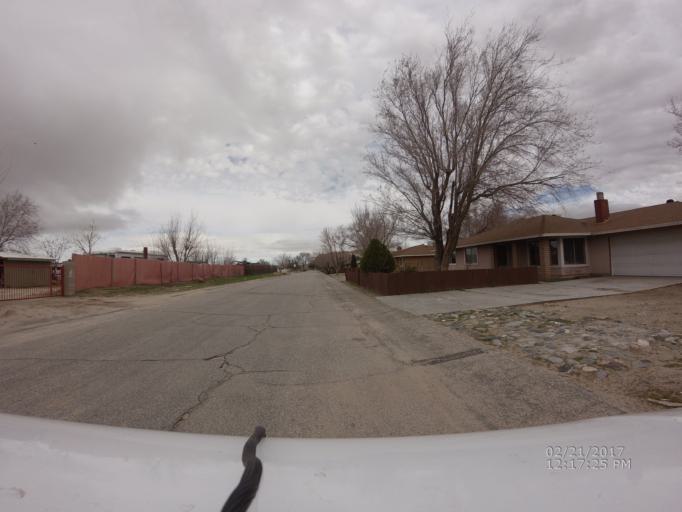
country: US
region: California
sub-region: Los Angeles County
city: Lake Los Angeles
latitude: 34.6329
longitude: -117.8555
